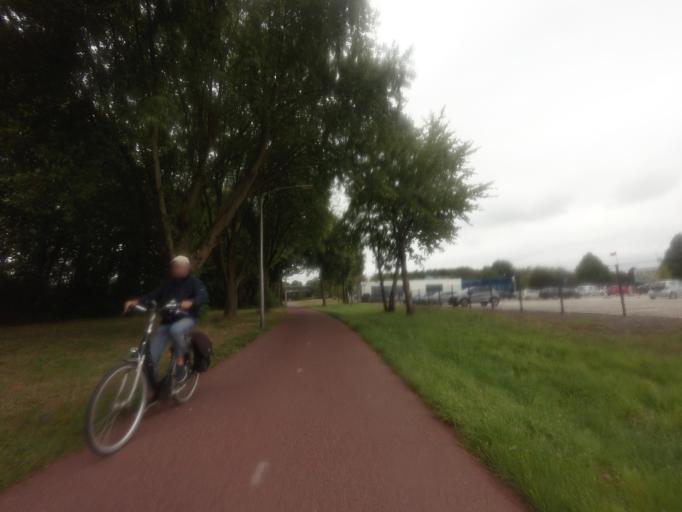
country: NL
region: Gelderland
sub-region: Gemeente Nijmegen
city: Lindenholt
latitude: 51.8395
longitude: 5.8095
